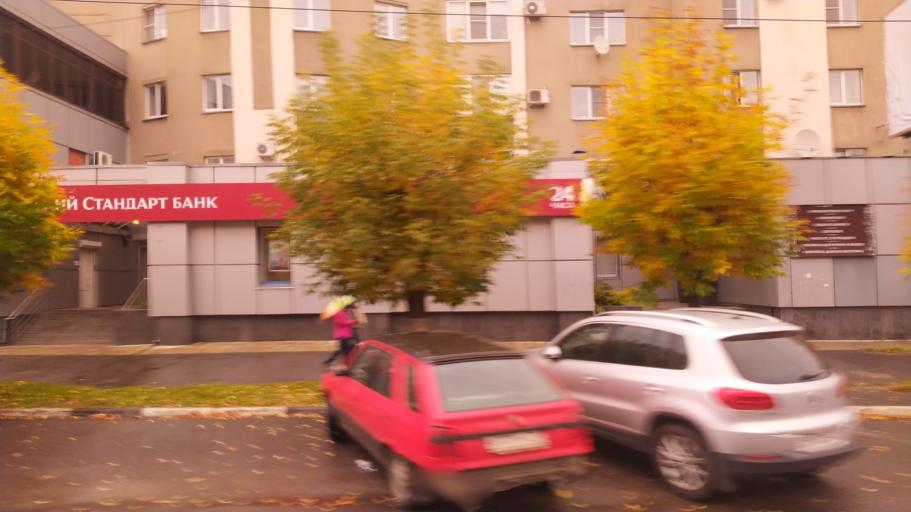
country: RU
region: Tverskaya
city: Tver
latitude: 56.8473
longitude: 35.9108
